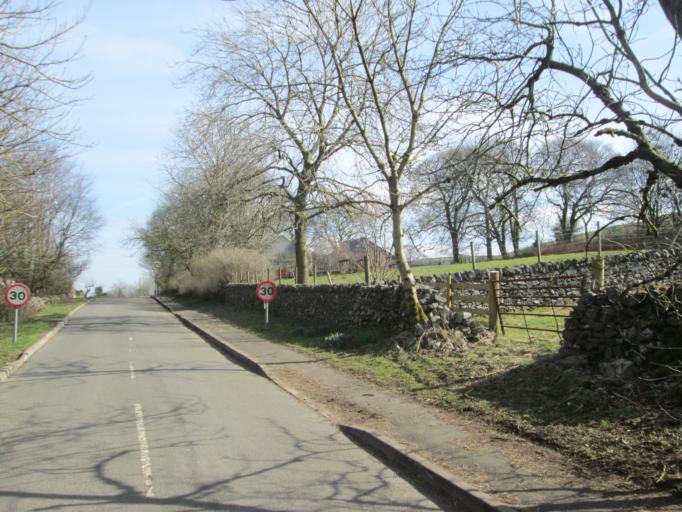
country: GB
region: England
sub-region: Derbyshire
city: Tideswell
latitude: 53.2383
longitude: -1.7963
